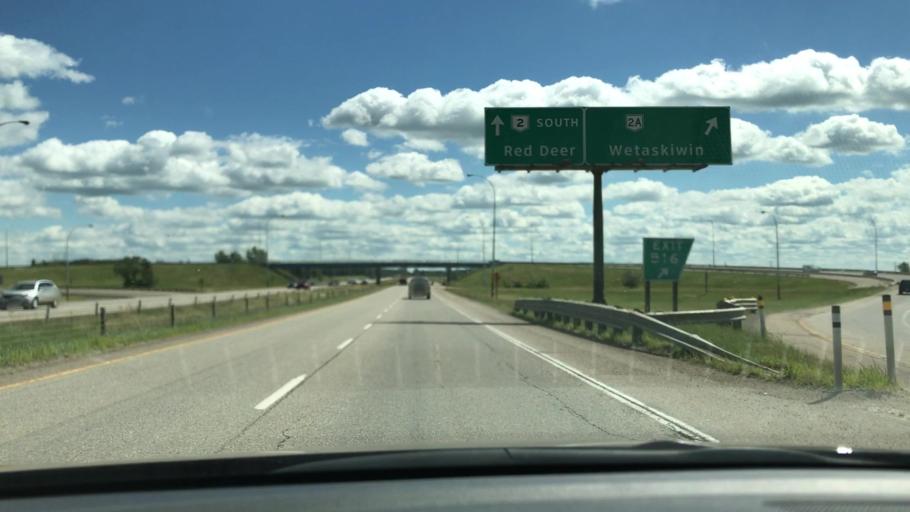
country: CA
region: Alberta
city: Leduc
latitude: 53.2551
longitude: -113.5619
